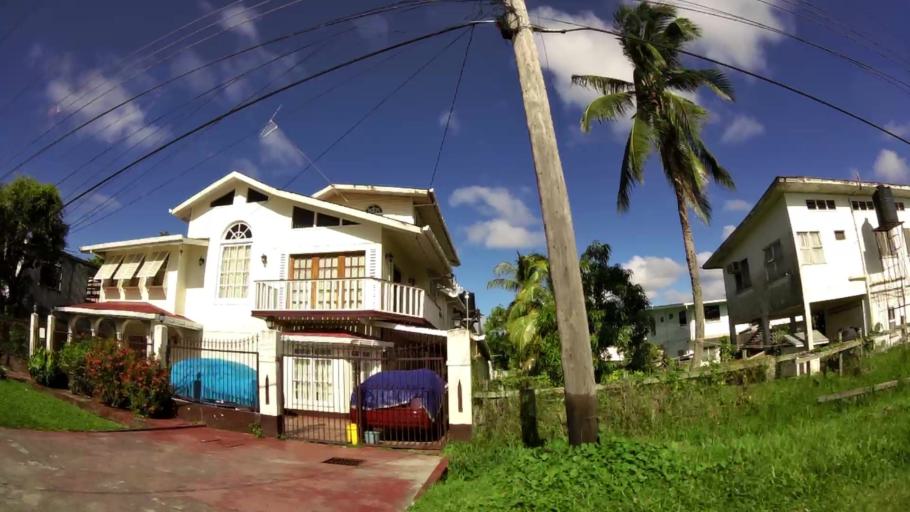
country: GY
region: Demerara-Mahaica
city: Georgetown
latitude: 6.8182
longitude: -58.1305
